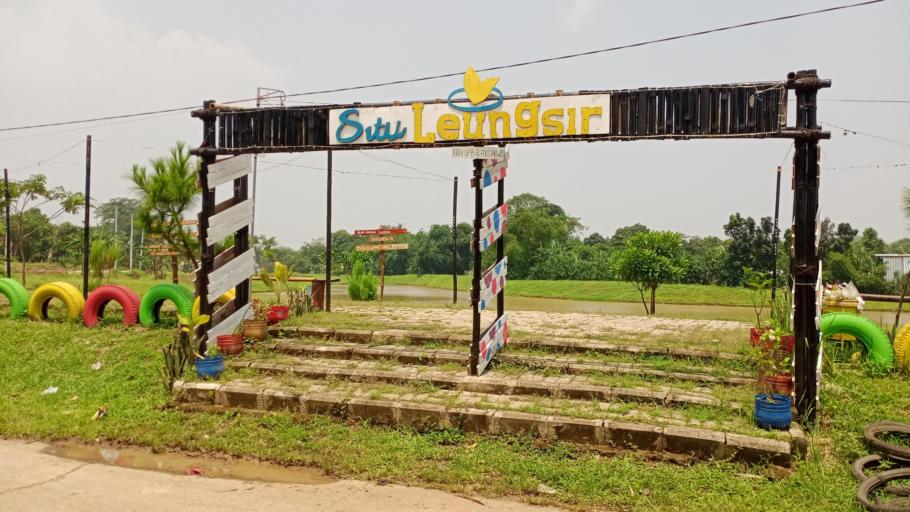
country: ID
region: West Java
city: Cileungsir
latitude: -6.3887
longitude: 107.0737
